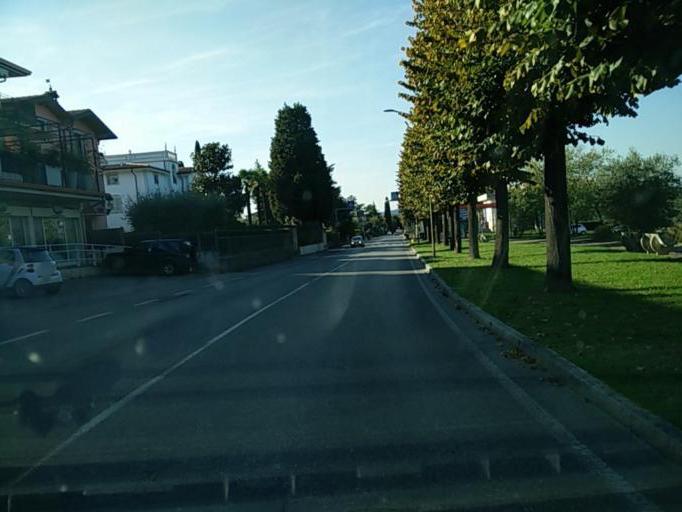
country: IT
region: Lombardy
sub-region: Provincia di Brescia
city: Desenzano del Garda
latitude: 45.4612
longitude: 10.5592
